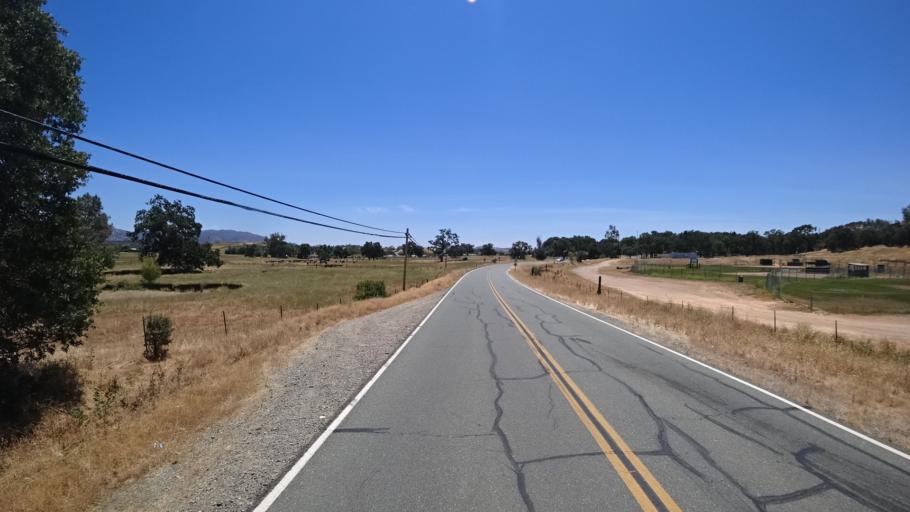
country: US
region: California
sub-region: Calaveras County
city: Valley Springs
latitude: 38.1973
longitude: -120.8264
